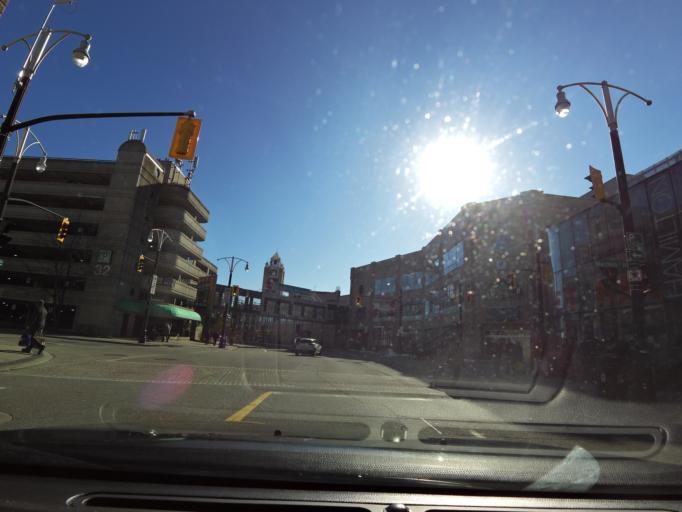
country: CA
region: Ontario
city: Hamilton
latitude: 43.2592
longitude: -79.8701
